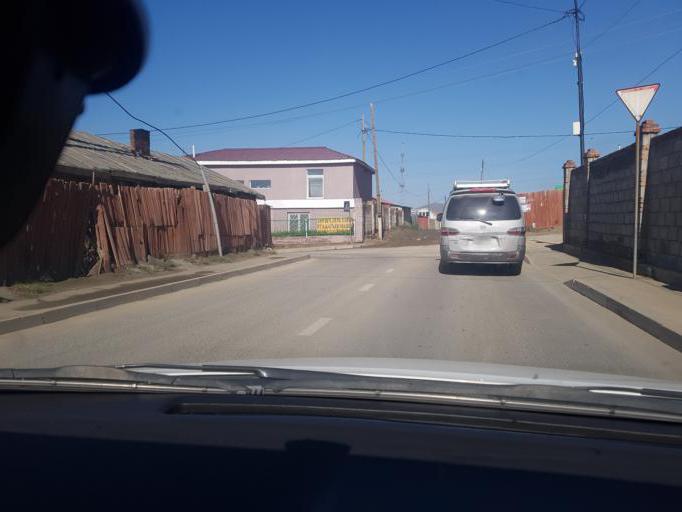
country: MN
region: Ulaanbaatar
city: Ulaanbaatar
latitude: 47.9508
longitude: 106.8616
